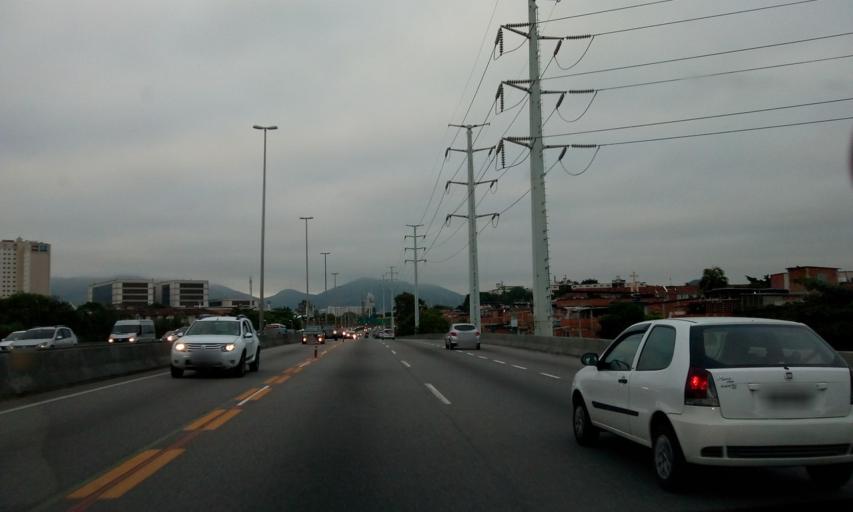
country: BR
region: Rio de Janeiro
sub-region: Rio De Janeiro
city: Rio de Janeiro
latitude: -22.8730
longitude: -43.2677
